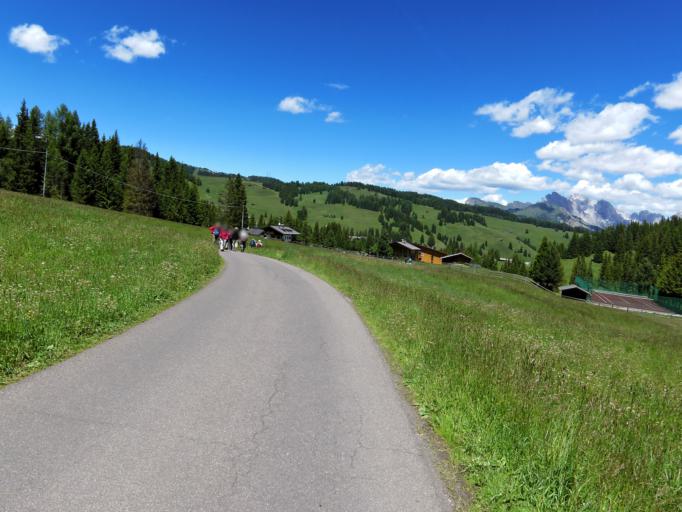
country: IT
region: Trentino-Alto Adige
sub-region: Bolzano
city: Ortisei
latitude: 46.5261
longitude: 11.6664
